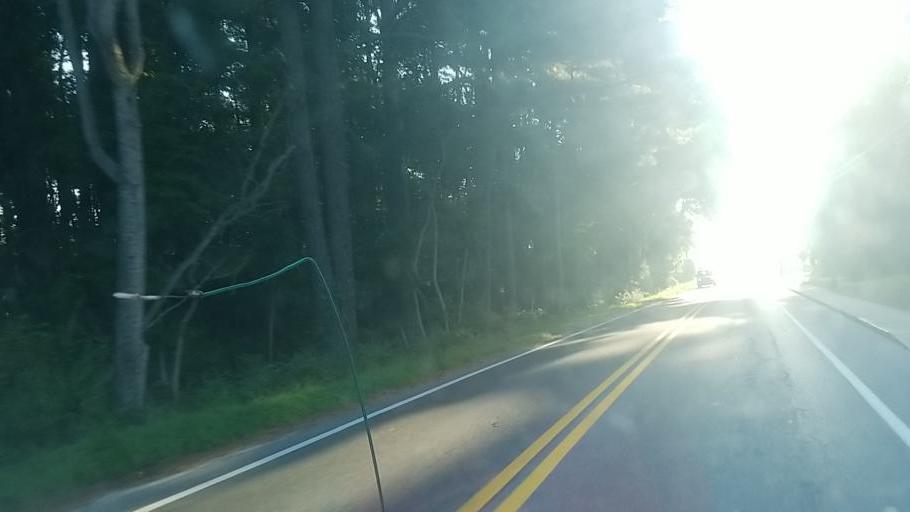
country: US
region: Delaware
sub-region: Sussex County
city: Selbyville
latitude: 38.4639
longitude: -75.2303
